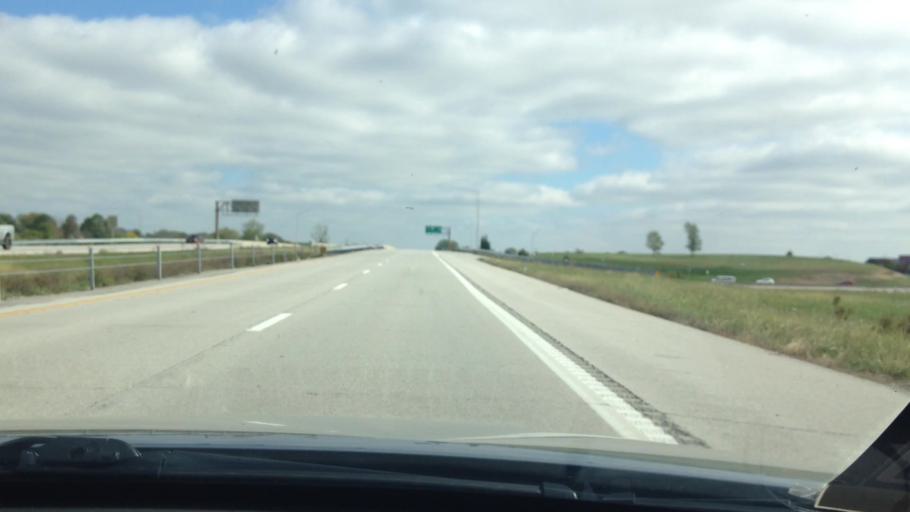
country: US
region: Missouri
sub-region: Platte County
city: Weatherby Lake
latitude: 39.2544
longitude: -94.6611
